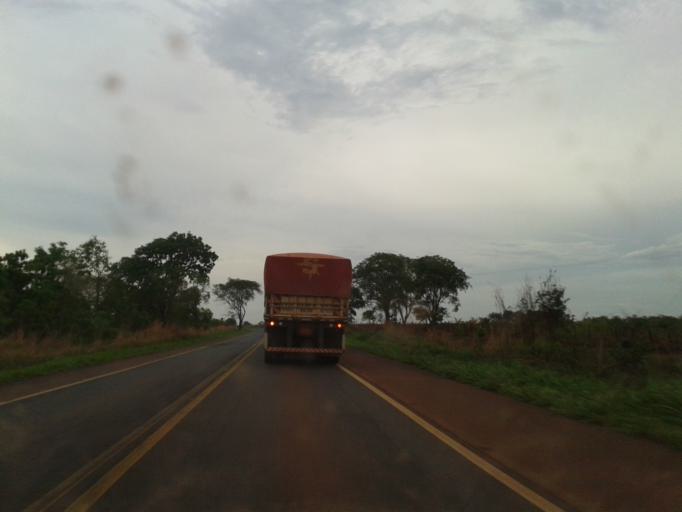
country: BR
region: Goias
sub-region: Santa Helena De Goias
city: Santa Helena de Goias
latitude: -17.9500
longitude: -50.5115
